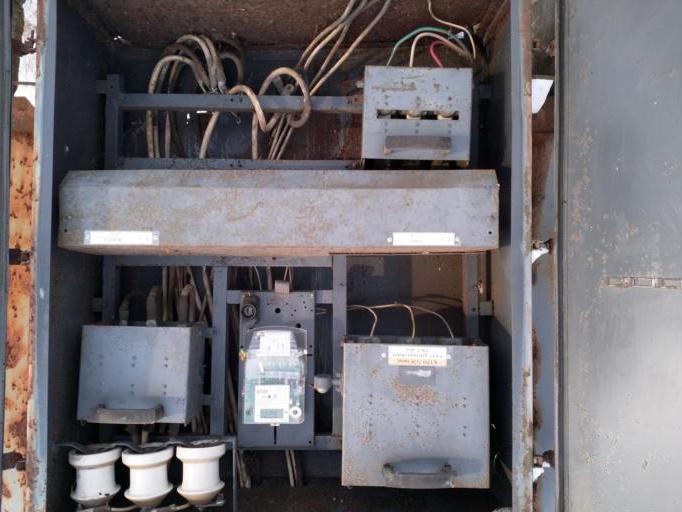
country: LV
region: Kuldigas Rajons
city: Kuldiga
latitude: 56.8636
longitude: 21.8858
